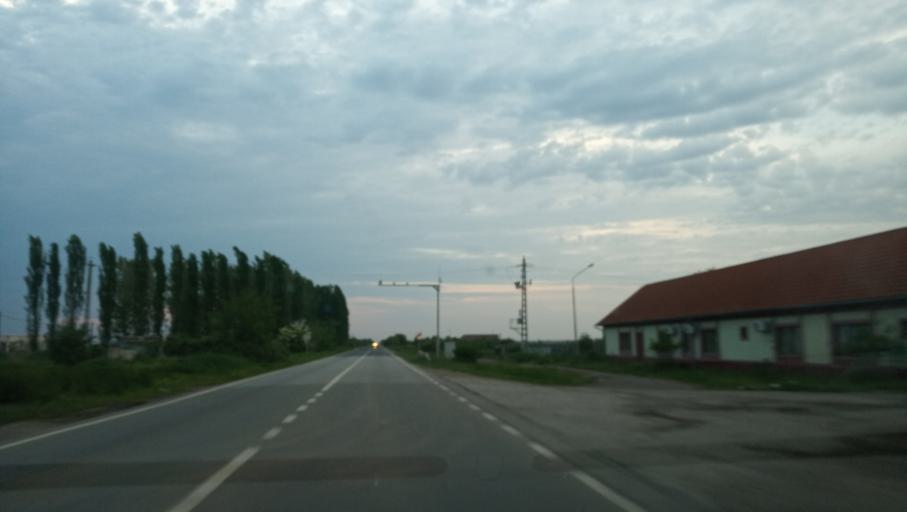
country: RO
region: Timis
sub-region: Comuna Jebel
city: Jebel
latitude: 45.5748
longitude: 21.2033
